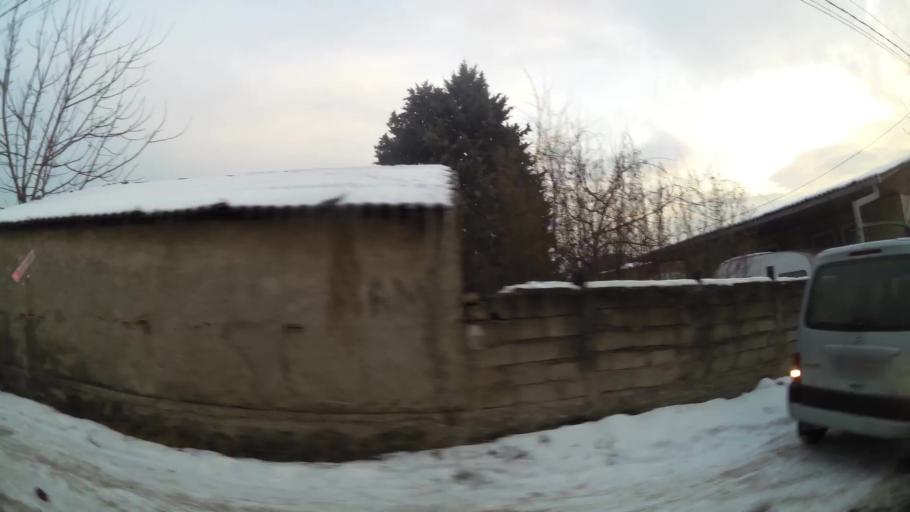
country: MK
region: Suto Orizari
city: Suto Orizare
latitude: 42.0376
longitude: 21.4095
